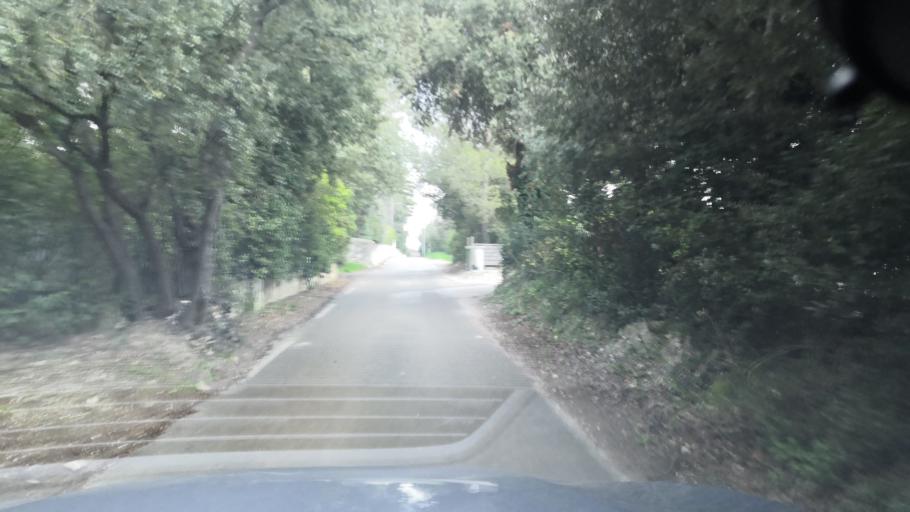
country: FR
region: Provence-Alpes-Cote d'Azur
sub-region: Departement des Bouches-du-Rhone
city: Aix-en-Provence
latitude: 43.5626
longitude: 5.4138
